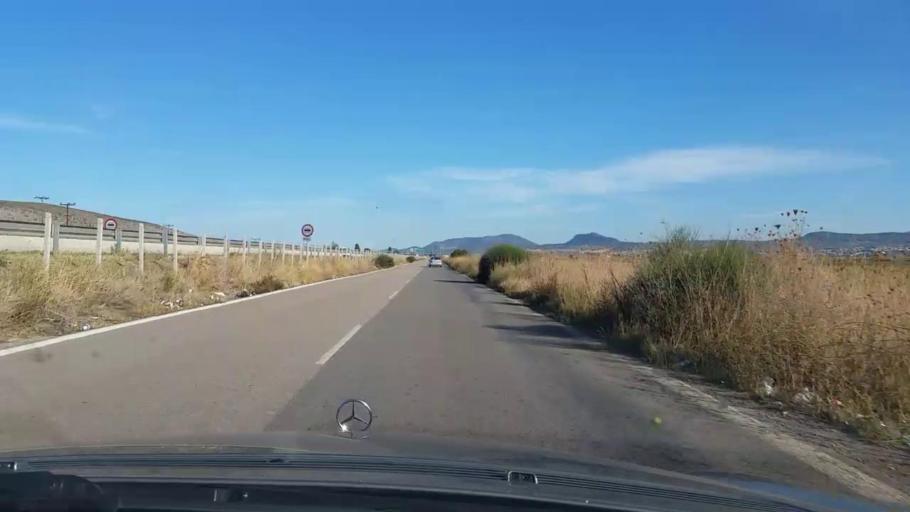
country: GR
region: Central Greece
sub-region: Nomos Voiotias
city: Thivai
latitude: 38.3735
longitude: 23.2750
